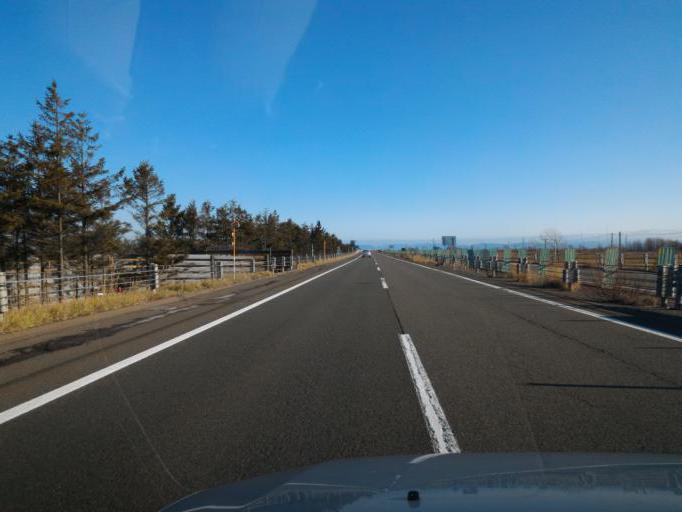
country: JP
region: Hokkaido
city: Ebetsu
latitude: 43.1087
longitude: 141.6075
